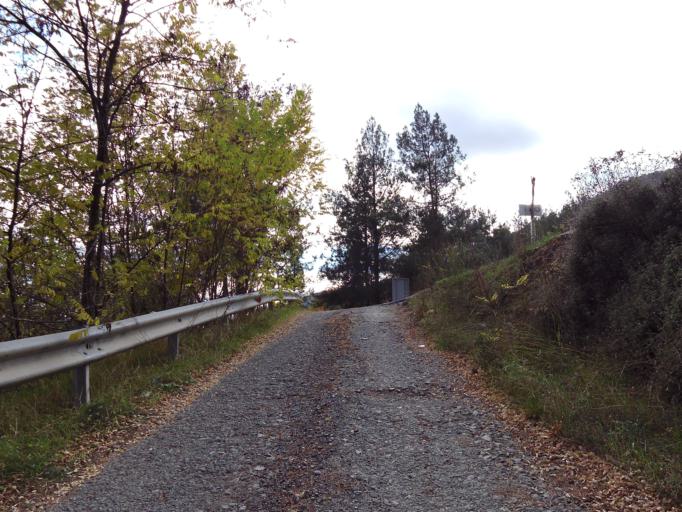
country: CY
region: Limassol
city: Kyperounta
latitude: 34.9306
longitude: 32.9355
